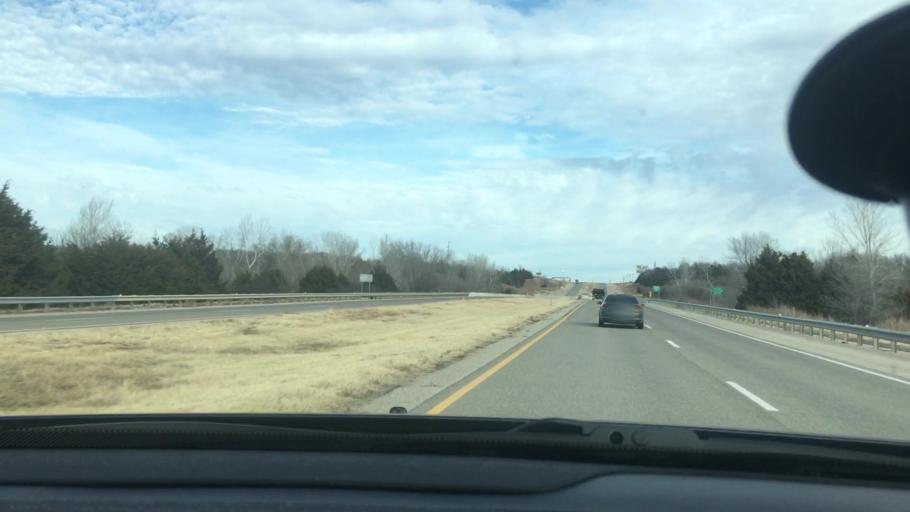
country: US
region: Oklahoma
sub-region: Pontotoc County
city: Byng
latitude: 34.9298
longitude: -96.6837
